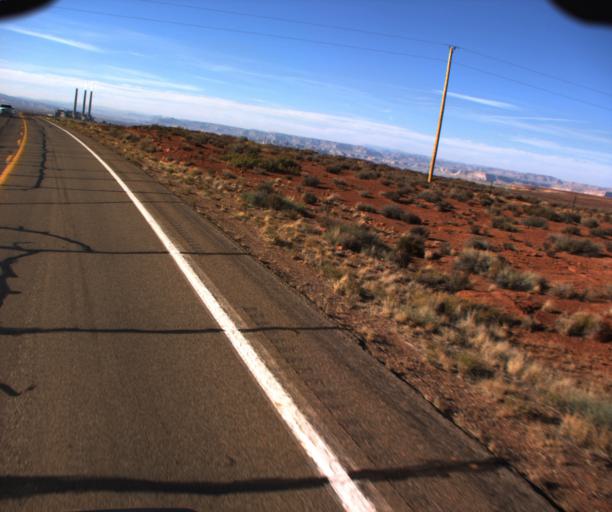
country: US
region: Arizona
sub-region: Coconino County
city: LeChee
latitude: 36.8794
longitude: -111.3460
